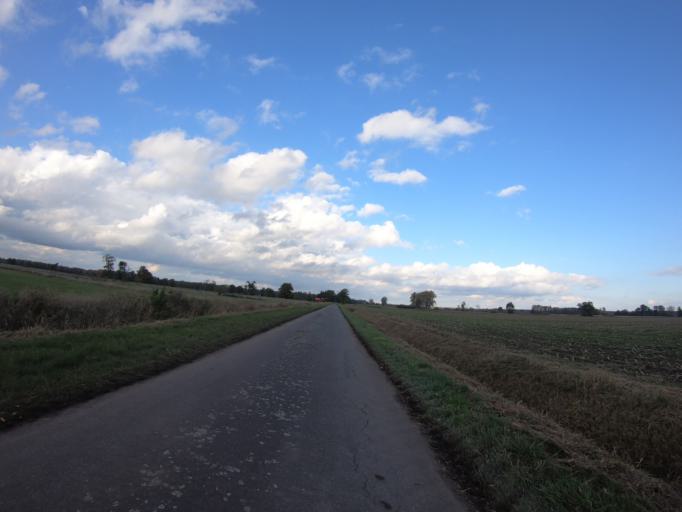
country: DE
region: Lower Saxony
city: Wagenhoff
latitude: 52.5338
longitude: 10.5480
